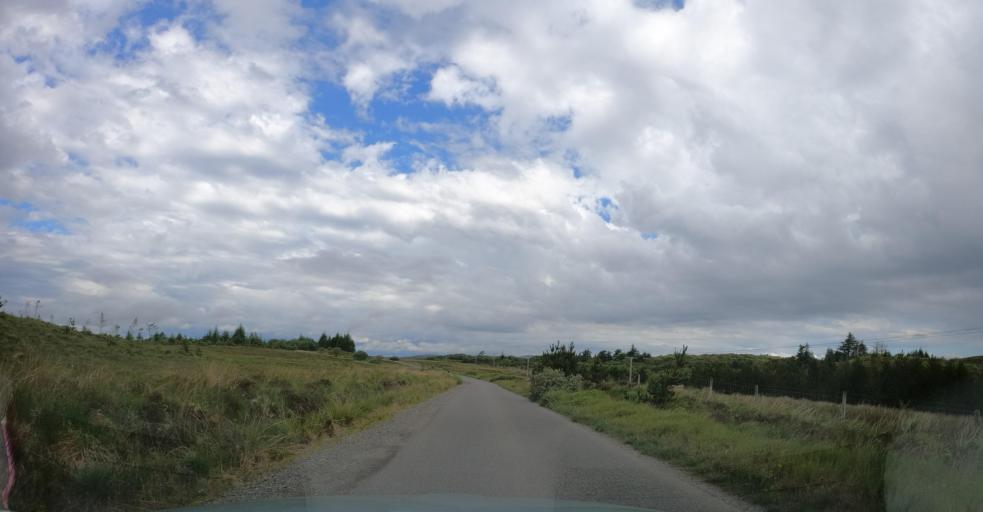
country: GB
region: Scotland
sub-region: Eilean Siar
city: Stornoway
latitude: 58.2023
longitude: -6.4116
